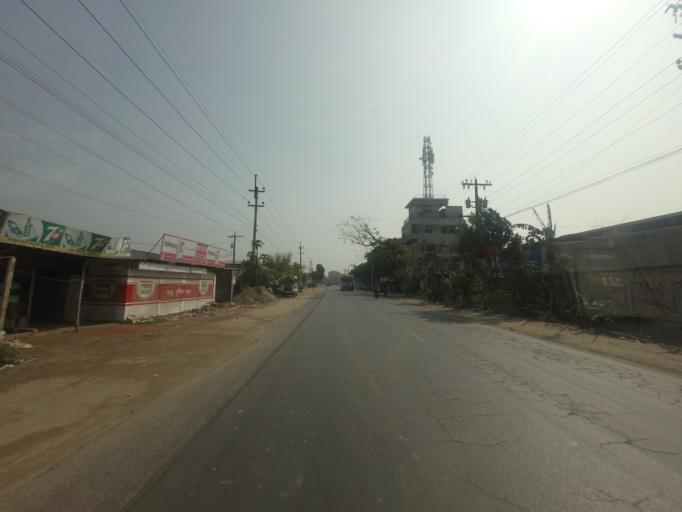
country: BD
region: Dhaka
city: Narsingdi
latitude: 23.8939
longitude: 90.6699
